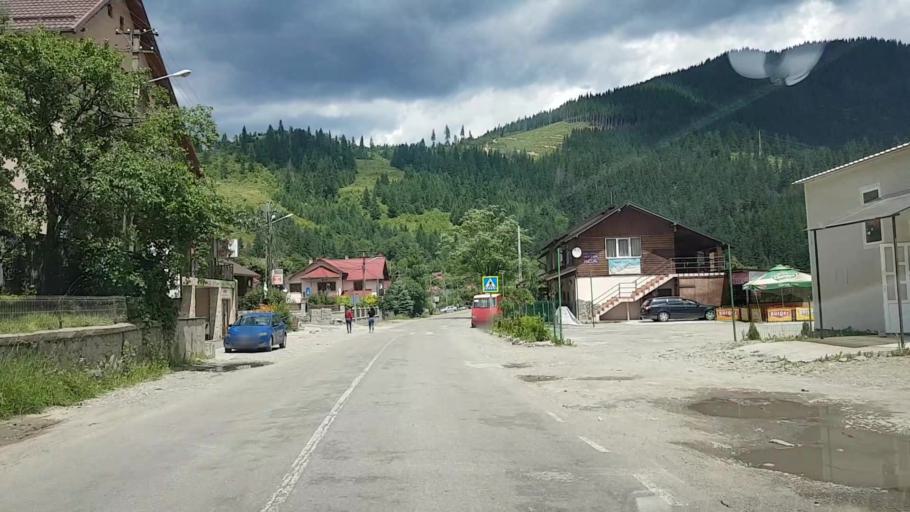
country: RO
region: Suceava
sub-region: Comuna Brosteni
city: Brosteni
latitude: 47.2392
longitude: 25.6990
